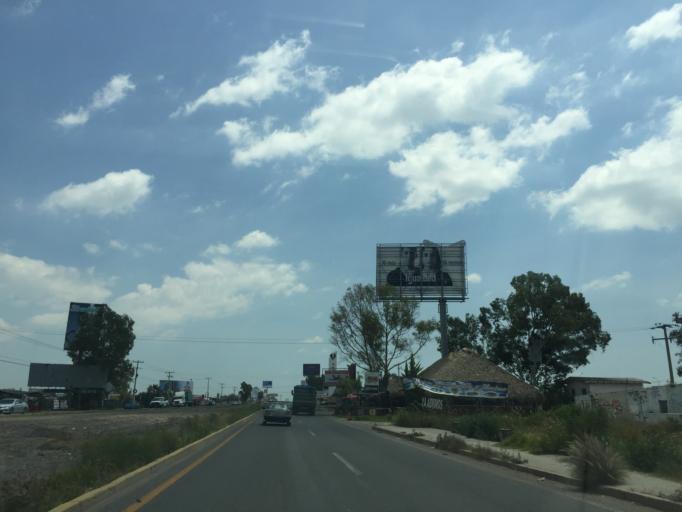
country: MX
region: Guanajuato
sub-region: Leon
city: Fraccionamiento Paseo de las Torres
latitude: 21.1877
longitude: -101.7463
